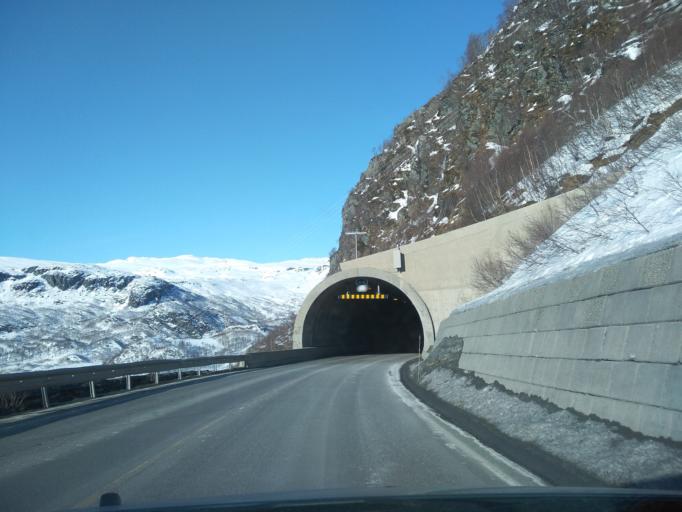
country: NO
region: Hordaland
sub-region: Odda
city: Odda
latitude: 59.8576
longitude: 6.8759
